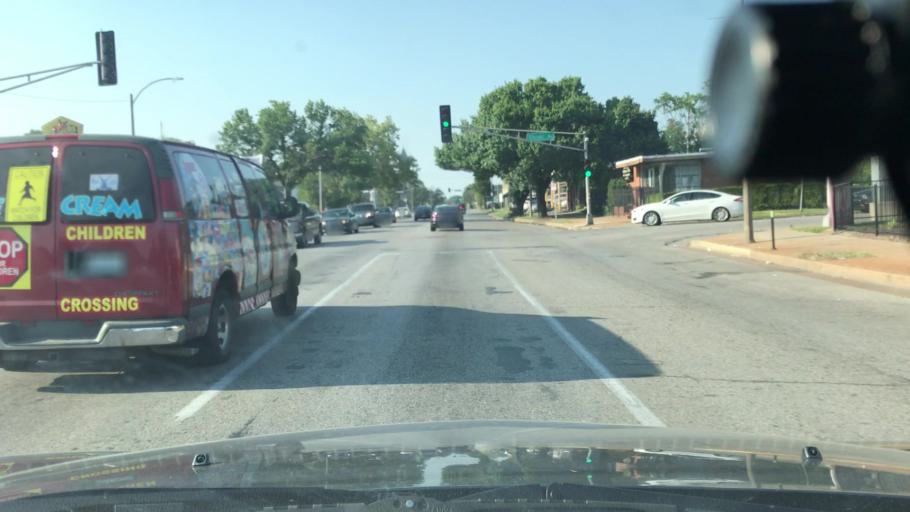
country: US
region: Missouri
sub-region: Saint Louis County
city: Hillsdale
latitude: 38.6524
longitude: -90.2633
